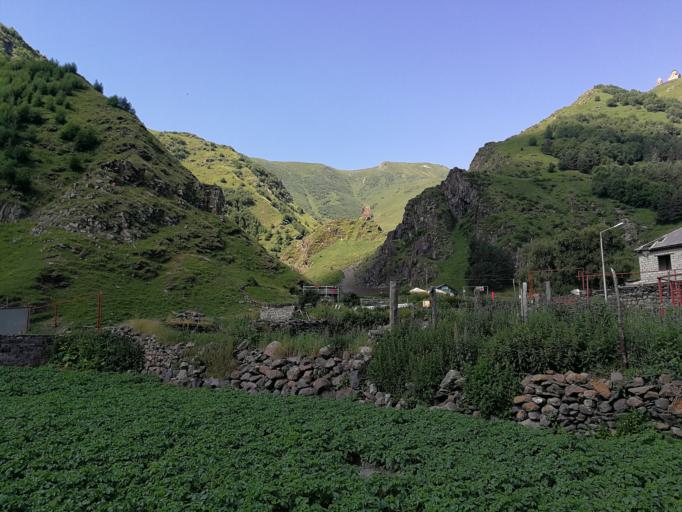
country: GE
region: Mtskheta-Mtianeti
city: Step'antsminda
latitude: 42.6626
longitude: 44.6305
